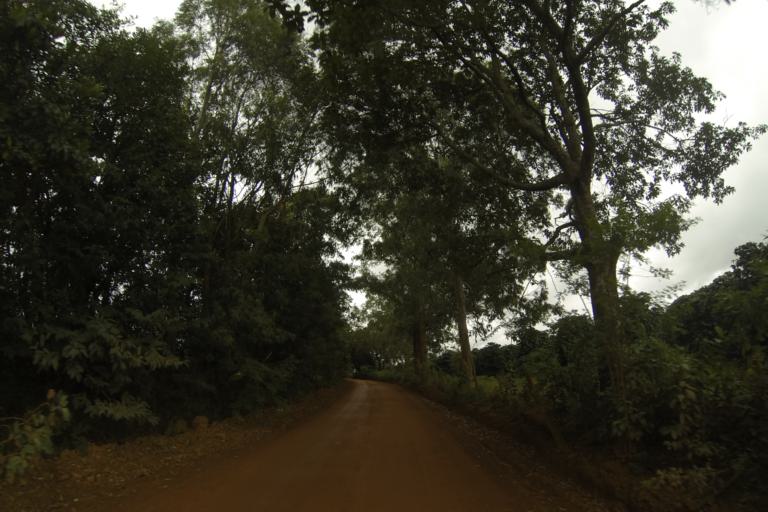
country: BR
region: Minas Gerais
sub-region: Campos Altos
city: Campos Altos
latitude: -19.8639
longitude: -46.3070
